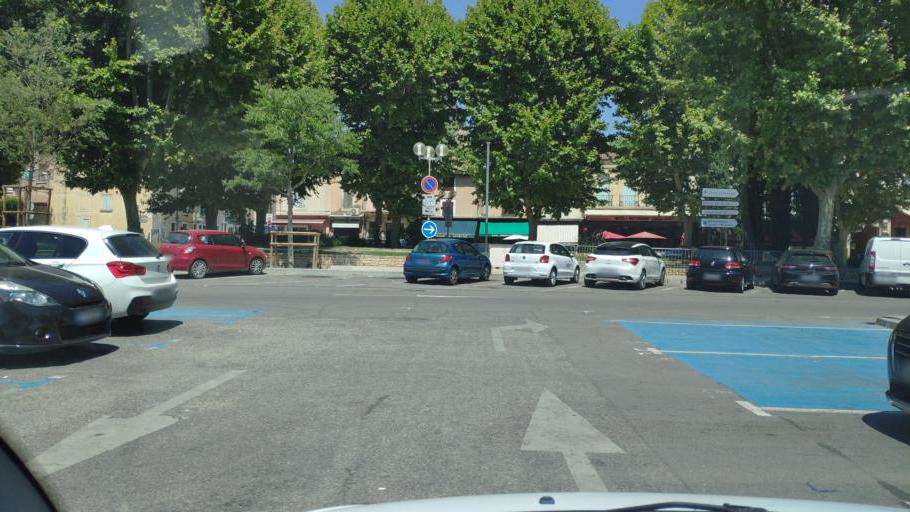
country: FR
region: Provence-Alpes-Cote d'Azur
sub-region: Departement du Vaucluse
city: Cavaillon
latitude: 43.8344
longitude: 5.0355
